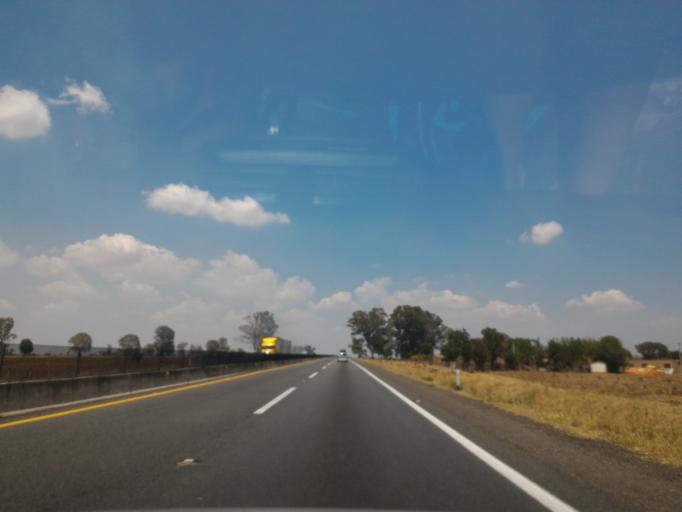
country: MX
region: Jalisco
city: Tepatitlan de Morelos
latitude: 20.8710
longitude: -102.7500
